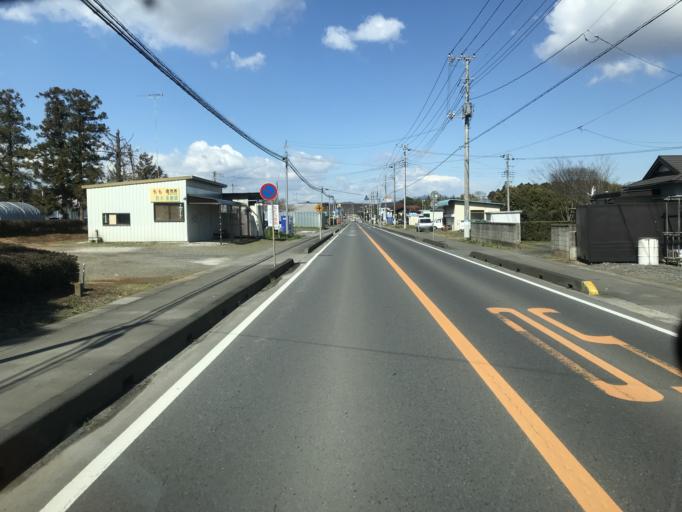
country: JP
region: Ibaraki
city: Ishioka
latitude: 36.1058
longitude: 140.2607
